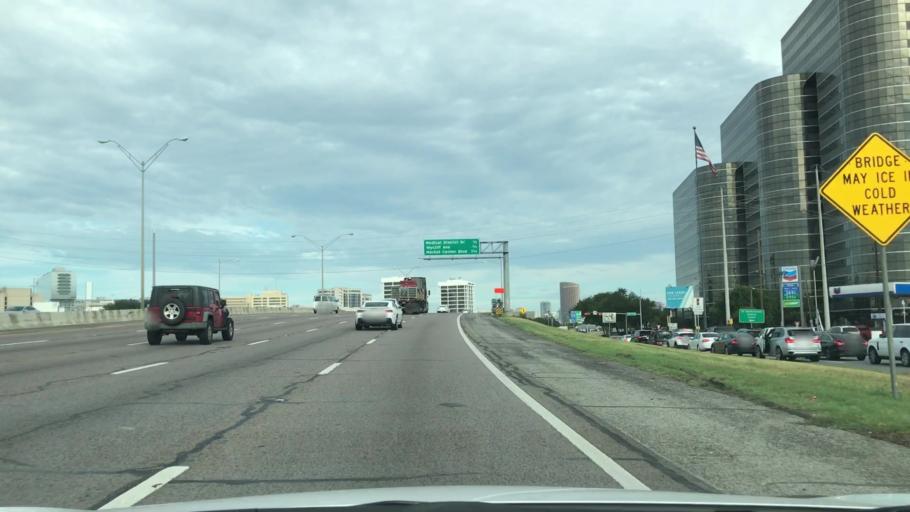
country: US
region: Texas
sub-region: Dallas County
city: Dallas
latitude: 32.8113
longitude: -96.8513
